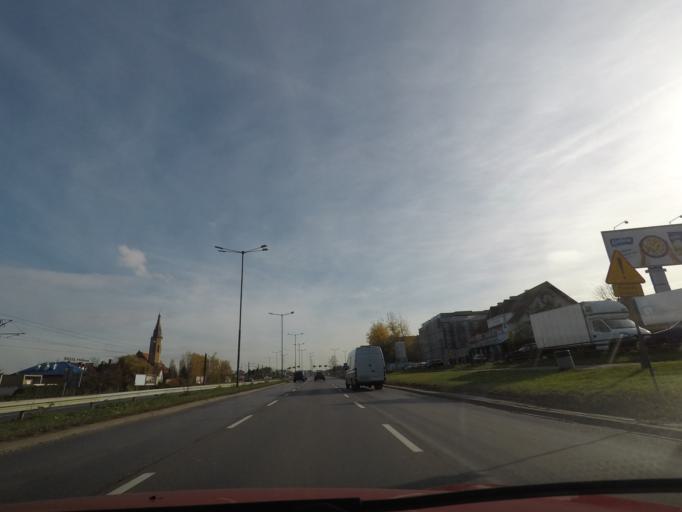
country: PL
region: Lesser Poland Voivodeship
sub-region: Krakow
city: Krakow
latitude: 50.0211
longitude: 19.9845
